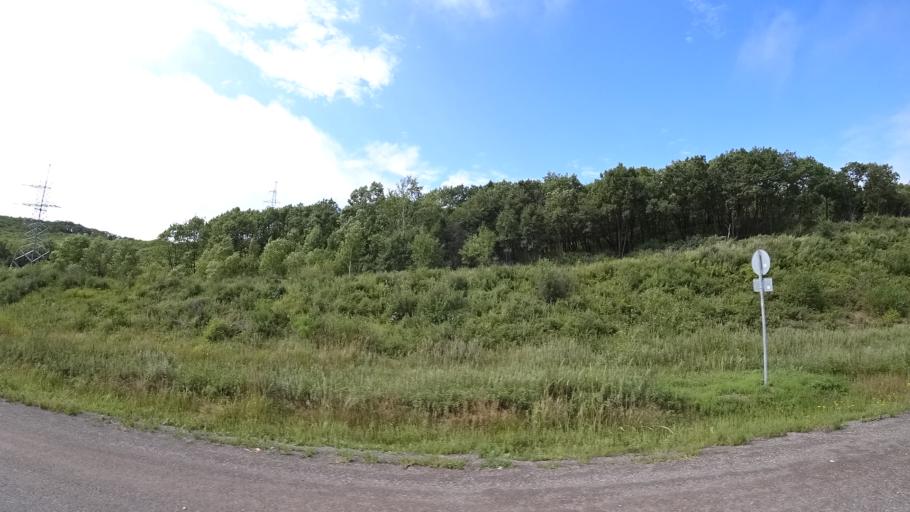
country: RU
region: Primorskiy
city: Lyalichi
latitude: 44.1226
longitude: 132.4215
